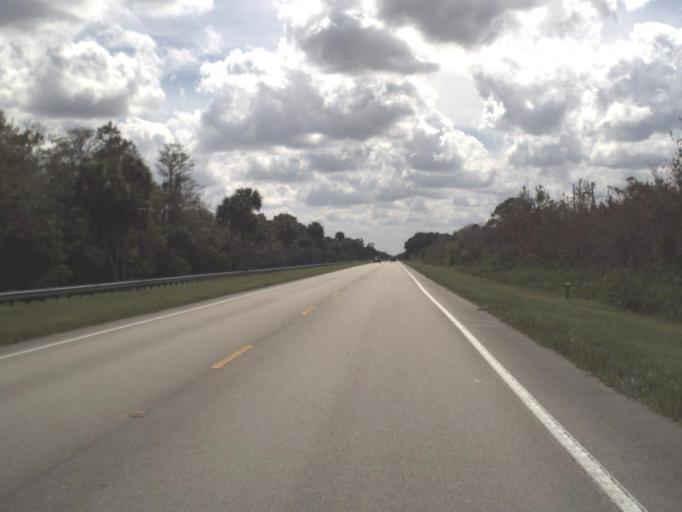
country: US
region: Florida
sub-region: Collier County
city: Orangetree
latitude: 26.1169
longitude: -81.3449
